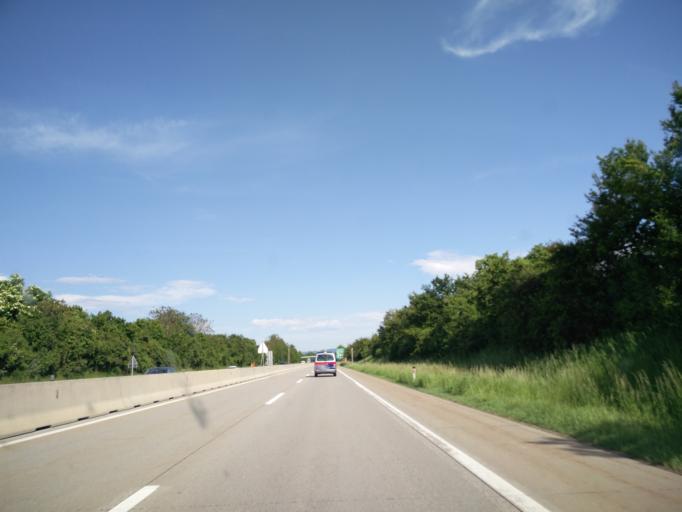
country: AT
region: Carinthia
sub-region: Politischer Bezirk Klagenfurt Land
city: Maria Saal
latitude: 46.6439
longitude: 14.3456
